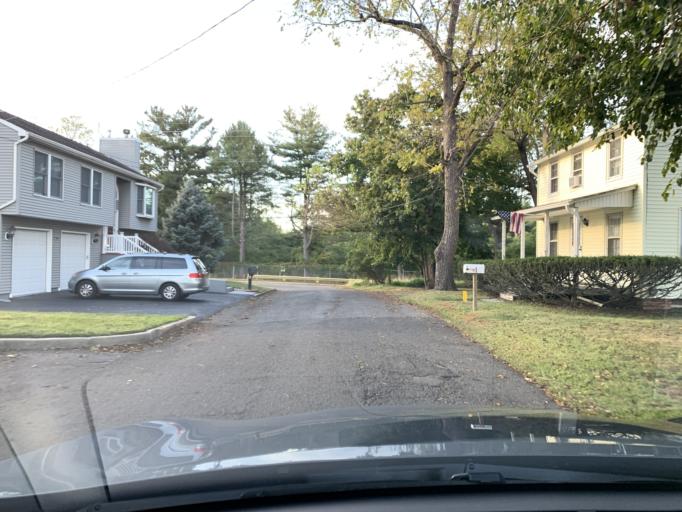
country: US
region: New Jersey
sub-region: Monmouth County
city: Eatontown
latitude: 40.3074
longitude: -74.0558
